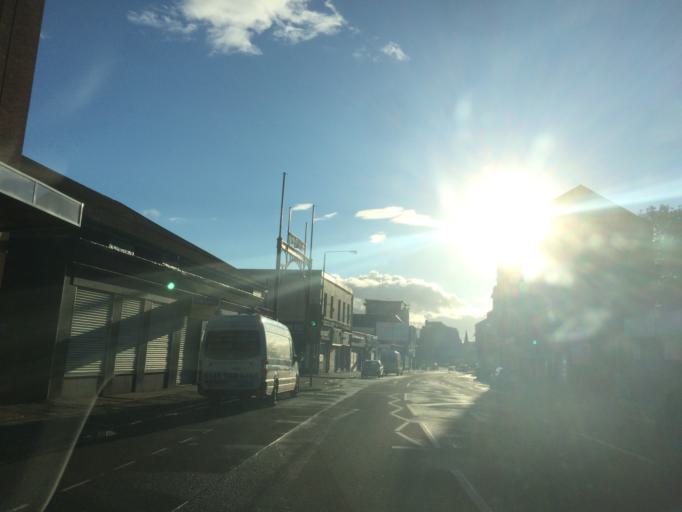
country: GB
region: Scotland
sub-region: Glasgow City
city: Glasgow
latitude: 55.8554
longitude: -4.2365
